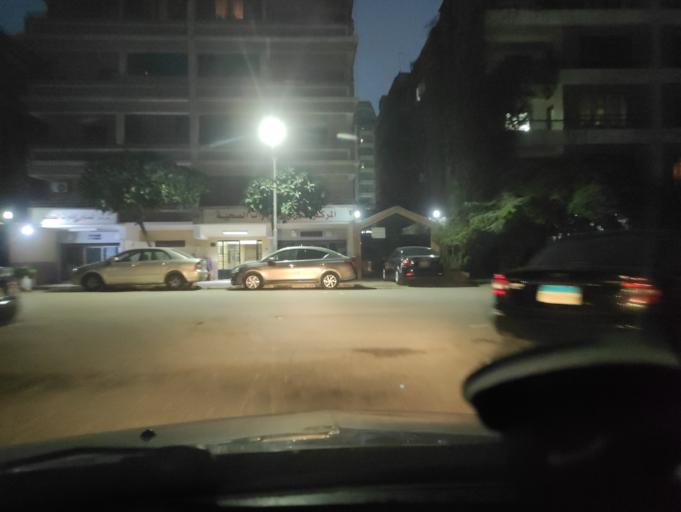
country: EG
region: Muhafazat al Qahirah
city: Cairo
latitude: 30.0451
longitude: 31.3346
